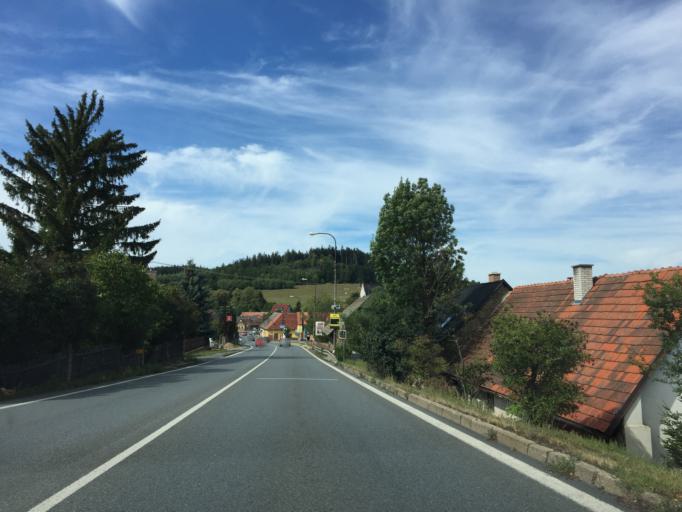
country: CZ
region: Central Bohemia
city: Votice
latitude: 49.5688
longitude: 14.6596
